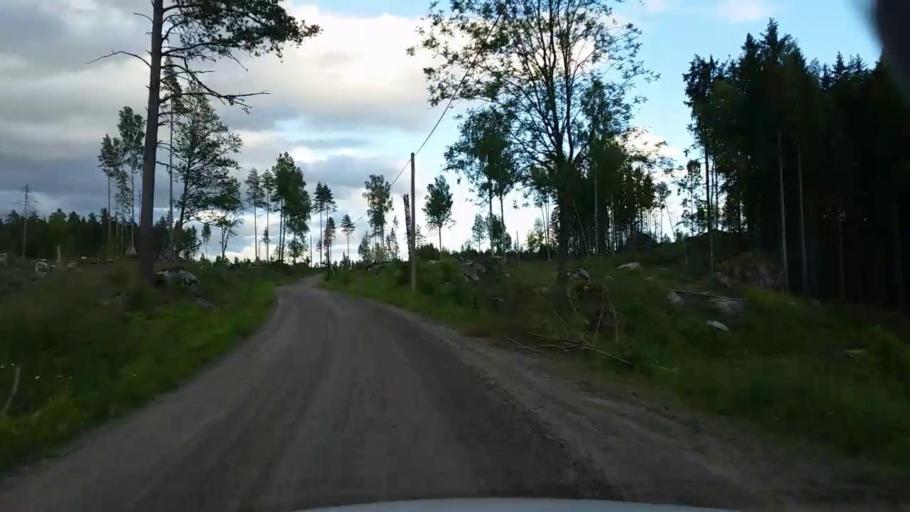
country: SE
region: Vaestmanland
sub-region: Kopings Kommun
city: Kolsva
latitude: 59.7754
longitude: 15.8757
